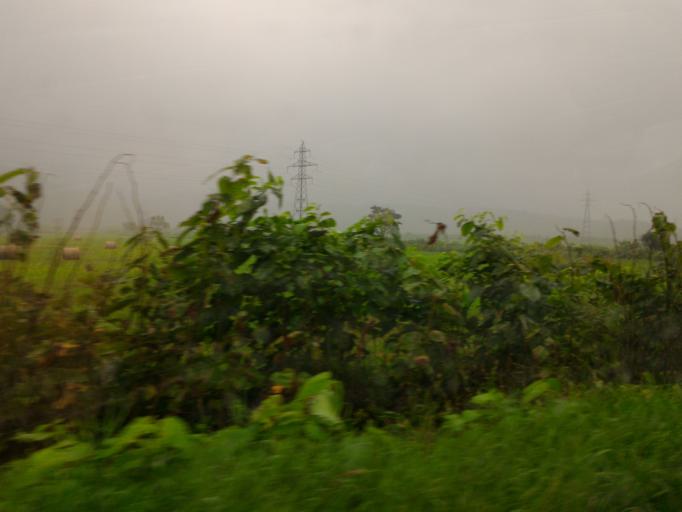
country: JP
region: Hokkaido
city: Makubetsu
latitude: 44.8554
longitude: 142.0565
